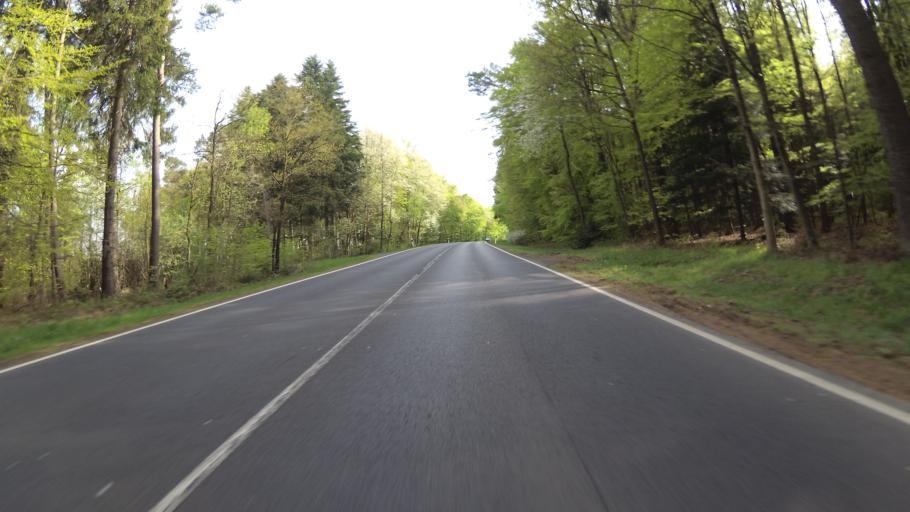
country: DE
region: Rheinland-Pfalz
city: Kelberg
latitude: 50.2813
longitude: 6.9222
